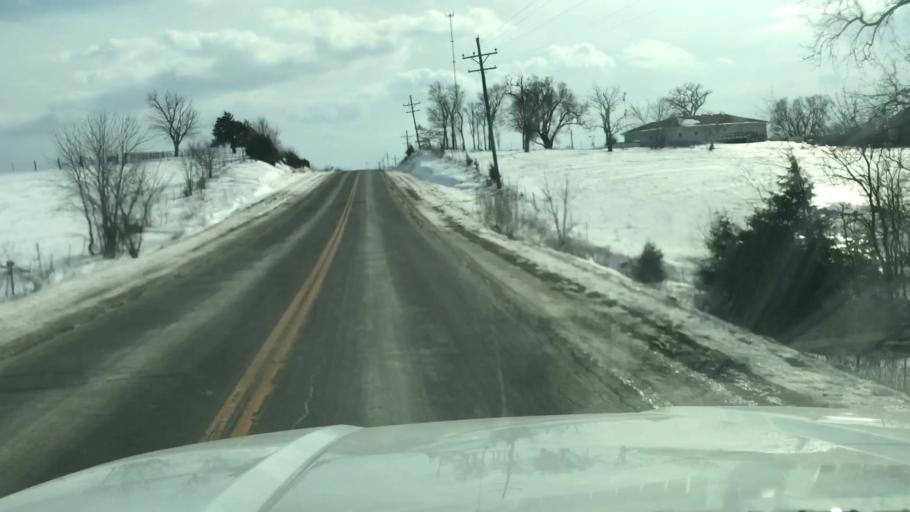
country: US
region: Missouri
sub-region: Gentry County
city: Stanberry
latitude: 40.3754
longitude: -94.6472
